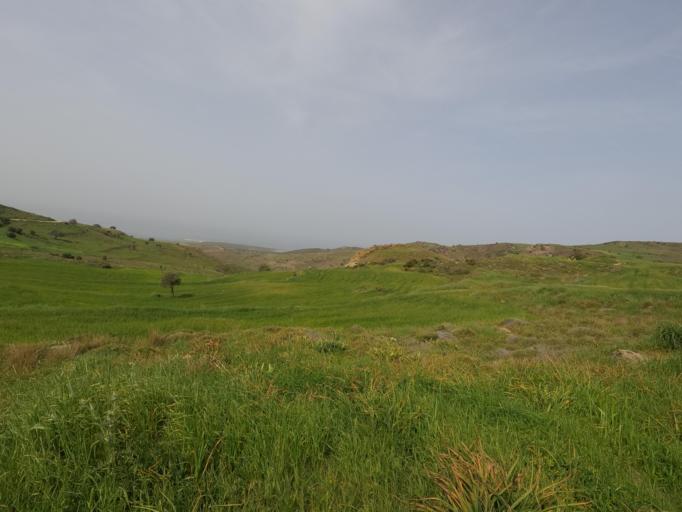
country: CY
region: Pafos
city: Pegeia
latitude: 34.9640
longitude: 32.3517
